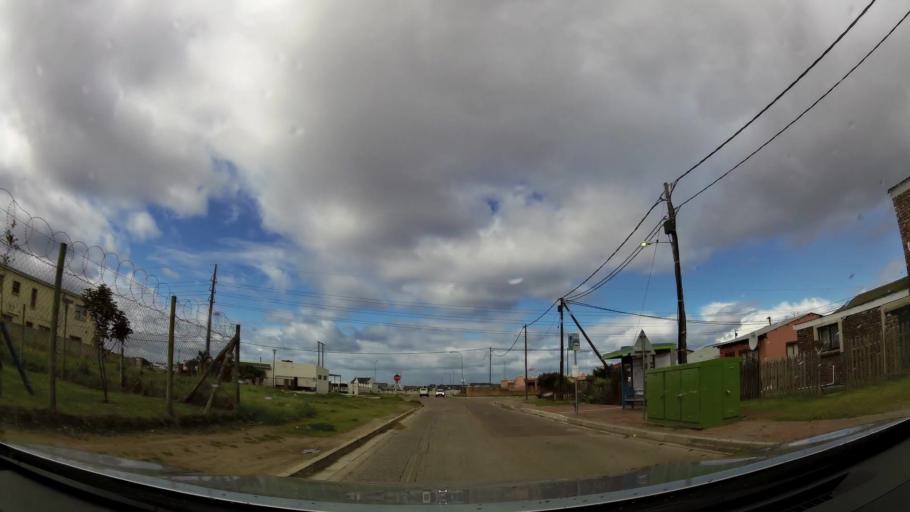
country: ZA
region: Western Cape
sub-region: Eden District Municipality
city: George
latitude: -33.9786
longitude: 22.4915
